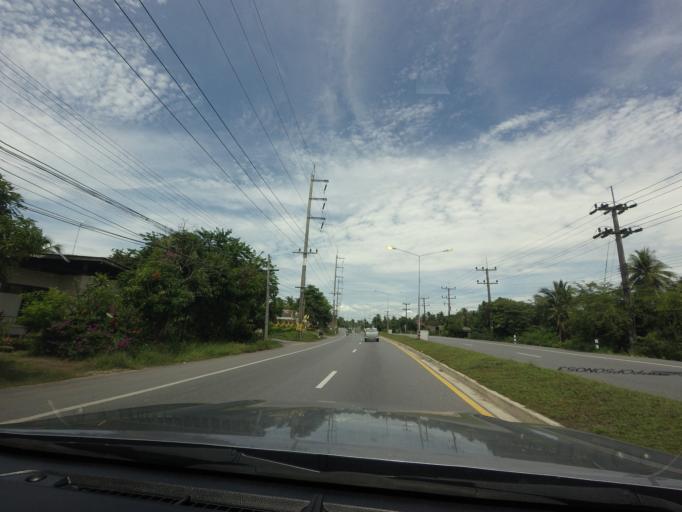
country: TH
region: Songkhla
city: Krasae Sin
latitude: 7.5990
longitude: 100.4018
